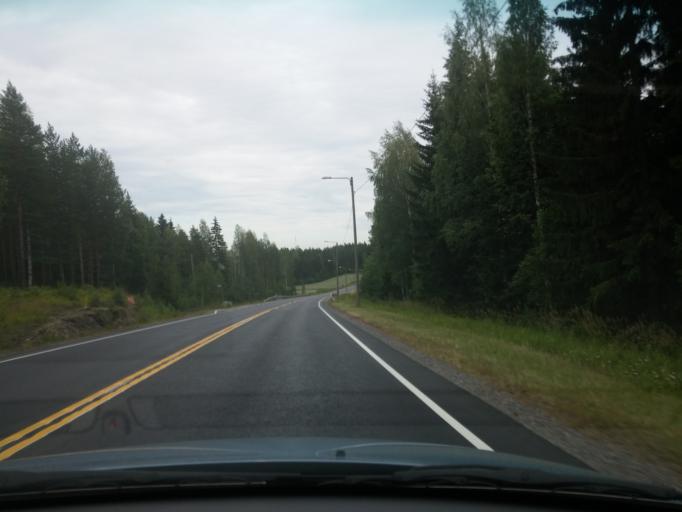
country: FI
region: Haeme
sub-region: Riihimaeki
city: Loppi
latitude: 60.7202
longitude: 24.4562
